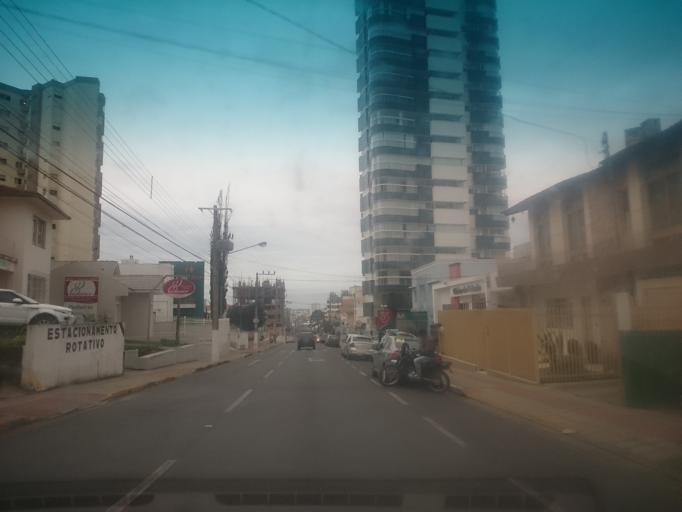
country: BR
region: Santa Catarina
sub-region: Lages
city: Lages
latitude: -27.8173
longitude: -50.3250
